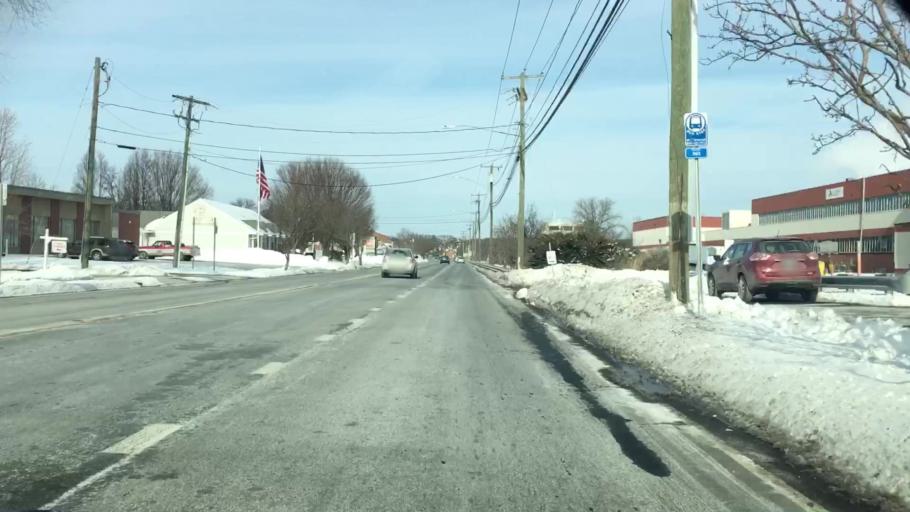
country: US
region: Connecticut
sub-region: Hartford County
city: Windsor Locks
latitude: 41.9256
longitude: -72.6273
